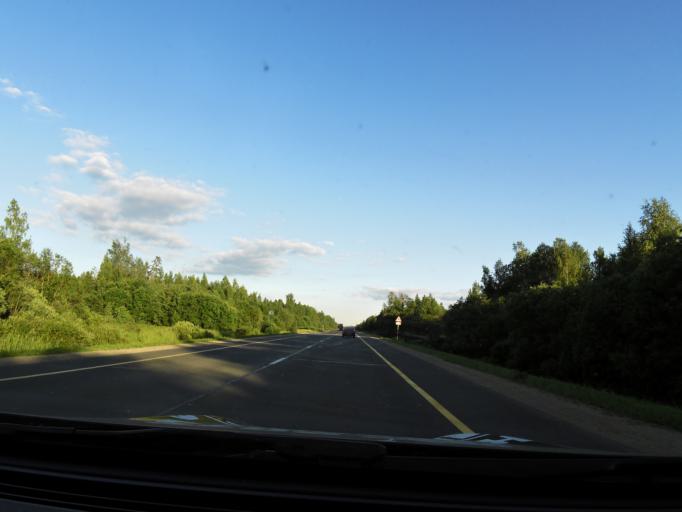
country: RU
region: Vologda
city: Vologda
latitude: 59.1040
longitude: 39.9882
